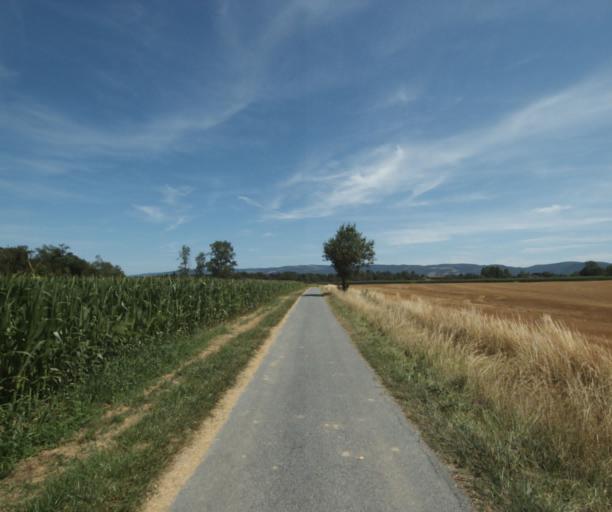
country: FR
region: Midi-Pyrenees
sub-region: Departement de la Haute-Garonne
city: Revel
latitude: 43.5087
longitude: 2.0175
